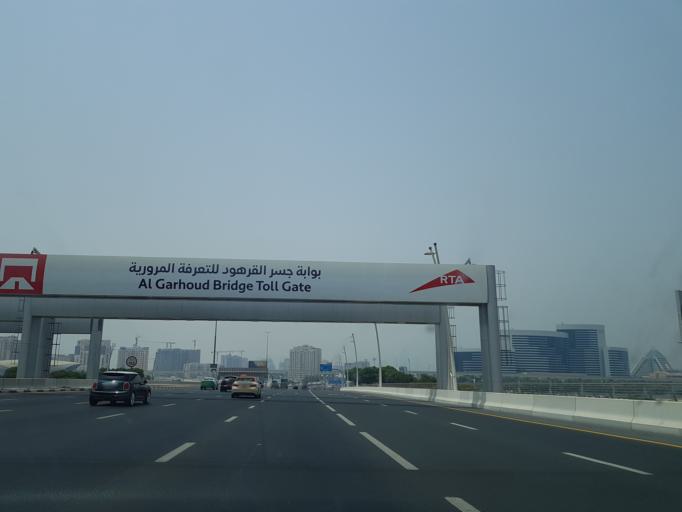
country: AE
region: Ash Shariqah
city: Sharjah
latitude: 25.2314
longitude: 55.3358
